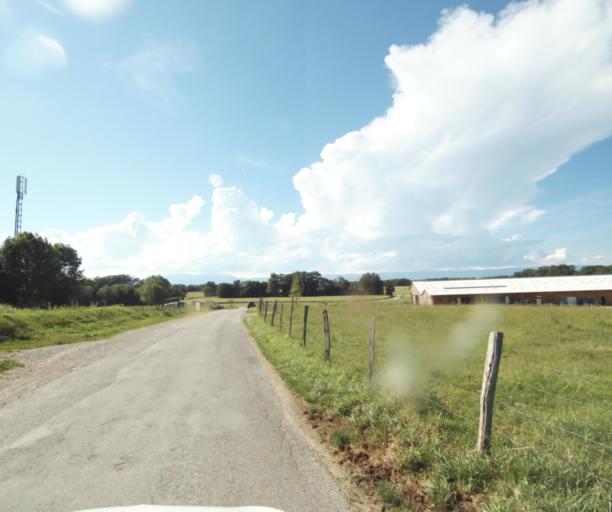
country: FR
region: Rhone-Alpes
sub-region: Departement de la Haute-Savoie
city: Massongy
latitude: 46.3249
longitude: 6.3173
